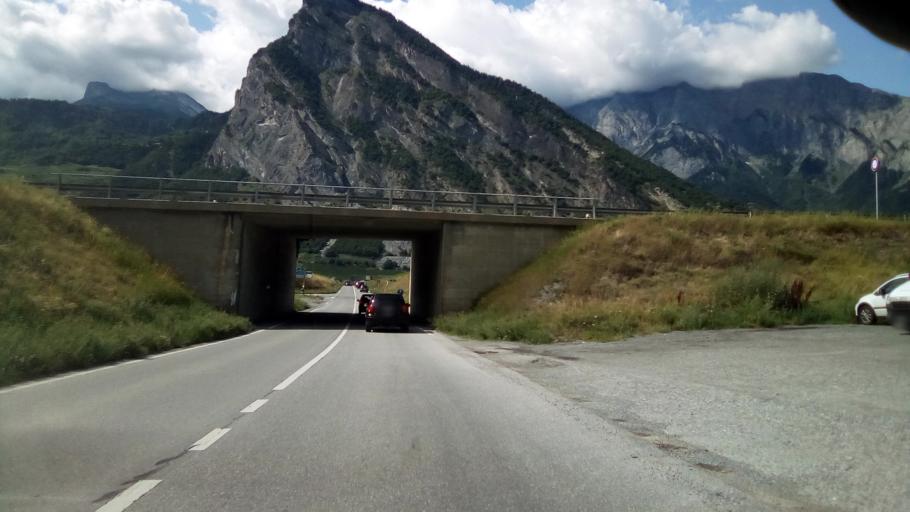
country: CH
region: Valais
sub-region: Martigny District
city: Riddes
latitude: 46.1808
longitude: 7.2170
